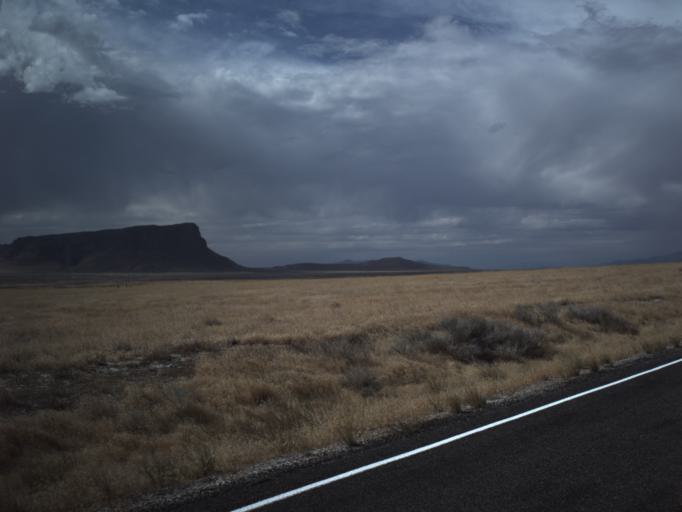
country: US
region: Utah
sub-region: Tooele County
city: Wendover
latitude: 41.3789
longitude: -113.9999
